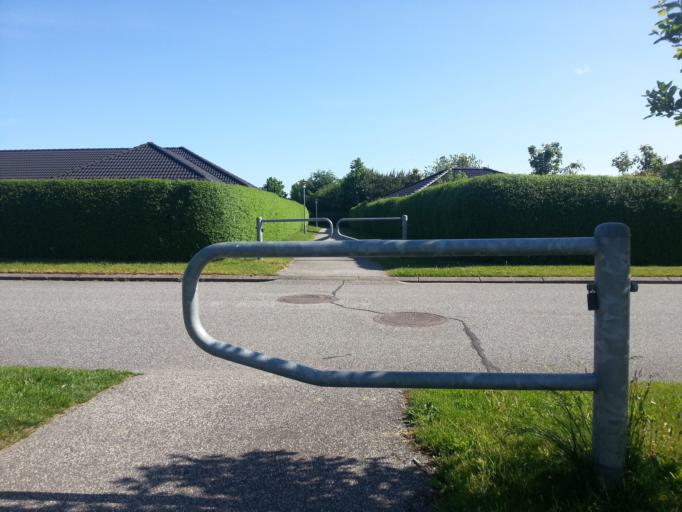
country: DK
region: North Denmark
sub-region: Alborg Kommune
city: Vadum
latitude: 57.1189
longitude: 9.8637
